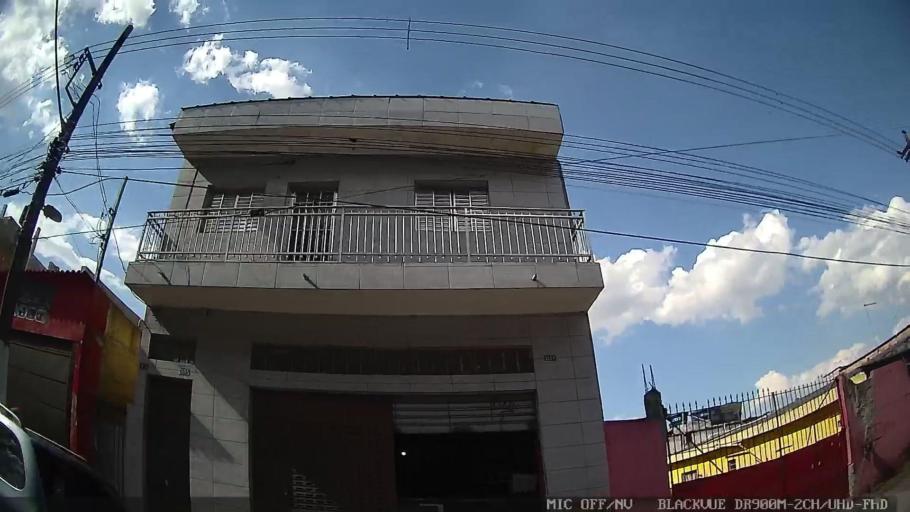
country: BR
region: Sao Paulo
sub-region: Ferraz De Vasconcelos
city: Ferraz de Vasconcelos
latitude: -23.5339
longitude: -46.3945
